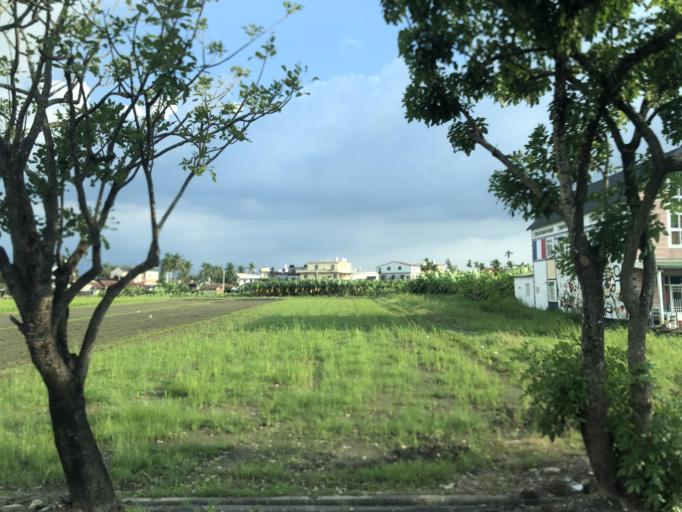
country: TW
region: Taiwan
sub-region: Pingtung
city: Pingtung
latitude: 22.8979
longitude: 120.5222
